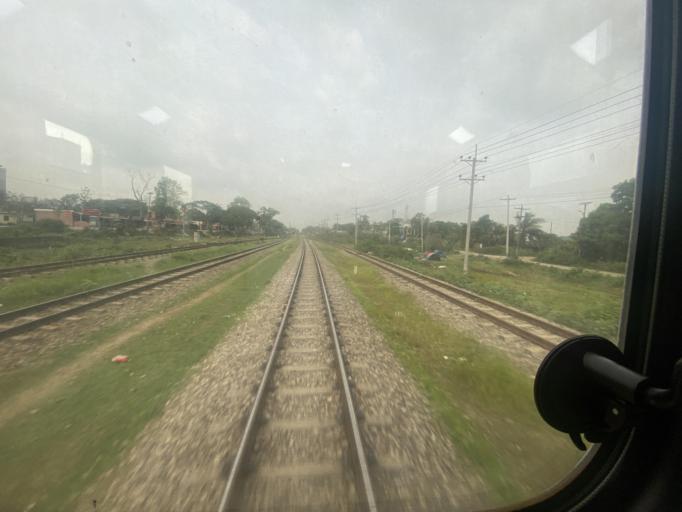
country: BD
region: Dhaka
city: Tungi
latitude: 23.9357
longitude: 90.4714
